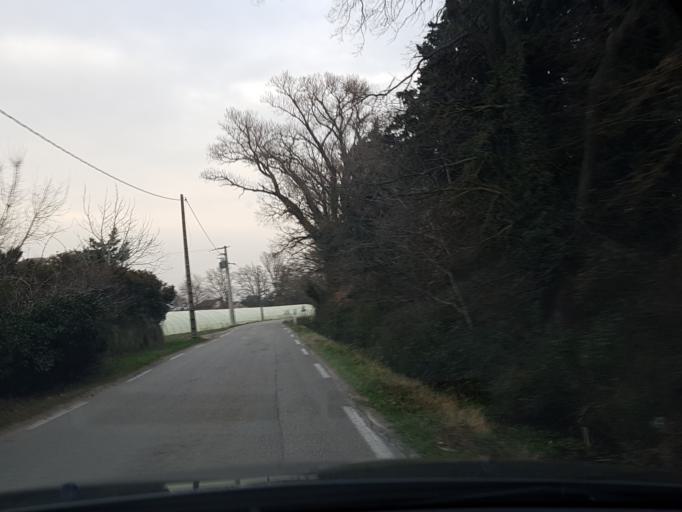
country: FR
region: Provence-Alpes-Cote d'Azur
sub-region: Departement du Vaucluse
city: Pernes-les-Fontaines
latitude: 44.0203
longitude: 5.0270
